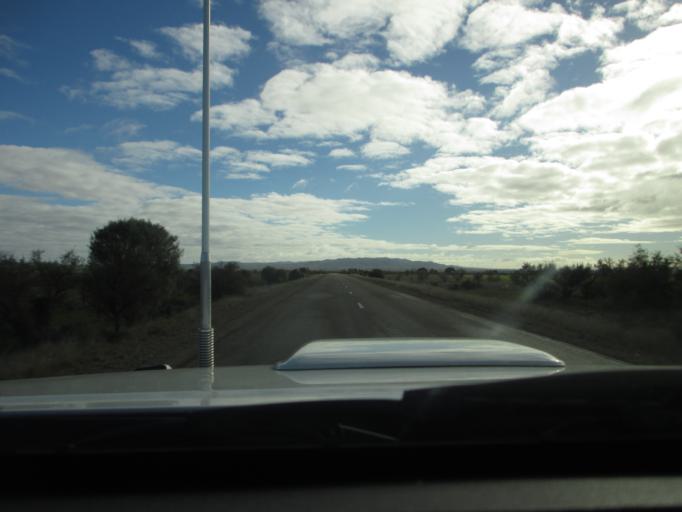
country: AU
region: South Australia
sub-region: Peterborough
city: Peterborough
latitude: -32.6975
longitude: 138.6098
